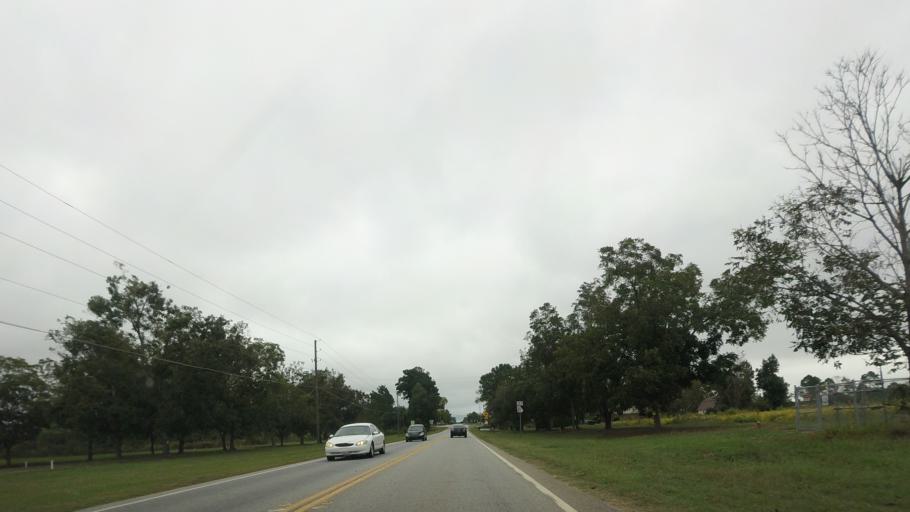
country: US
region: Georgia
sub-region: Berrien County
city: Ray City
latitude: 31.0227
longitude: -83.1980
